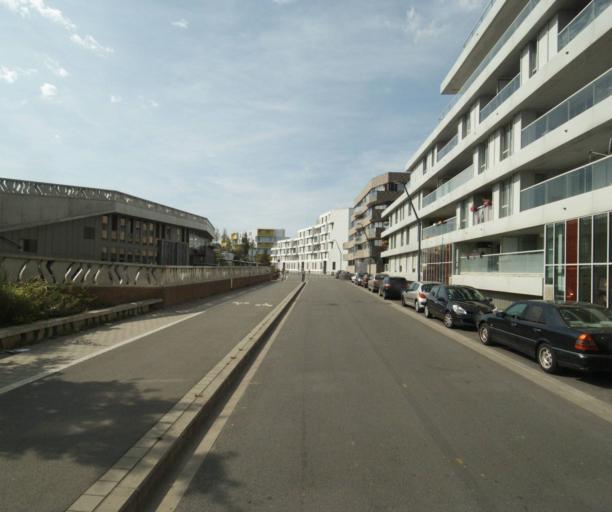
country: FR
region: Nord-Pas-de-Calais
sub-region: Departement du Nord
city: Lille
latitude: 50.6124
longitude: 3.0554
